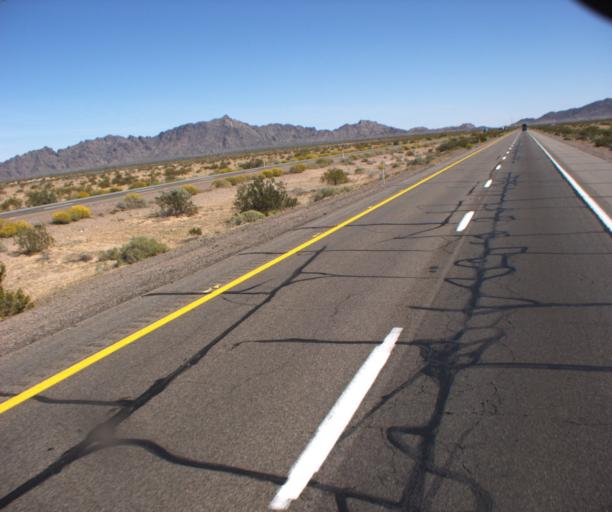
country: US
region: Arizona
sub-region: Yuma County
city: Wellton
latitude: 32.7133
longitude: -113.8218
